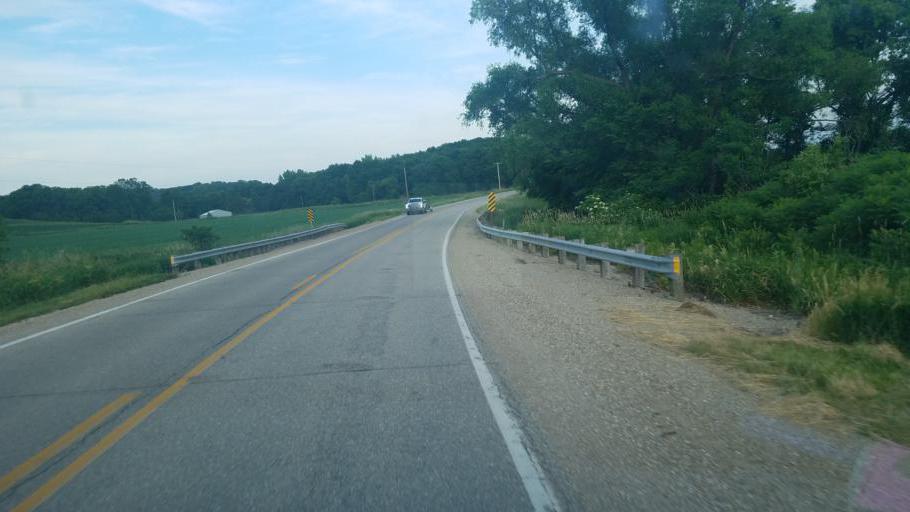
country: US
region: Iowa
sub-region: Tama County
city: Tama
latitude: 41.9587
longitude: -92.4286
